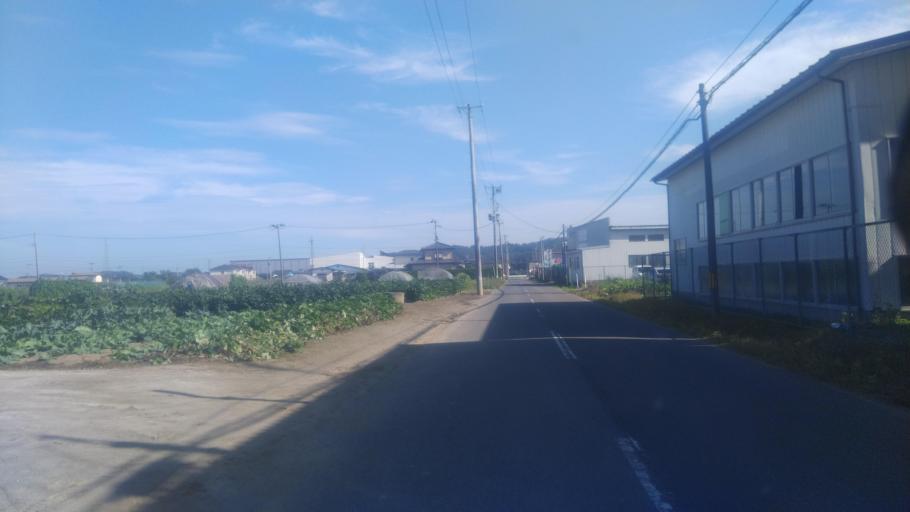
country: JP
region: Miyagi
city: Okawara
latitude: 38.0462
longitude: 140.7038
